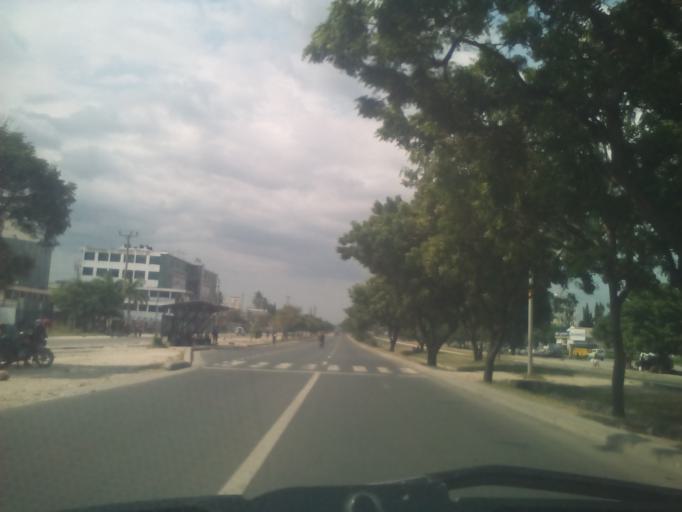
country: TZ
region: Dar es Salaam
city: Dar es Salaam
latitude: -6.8390
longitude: 39.2557
